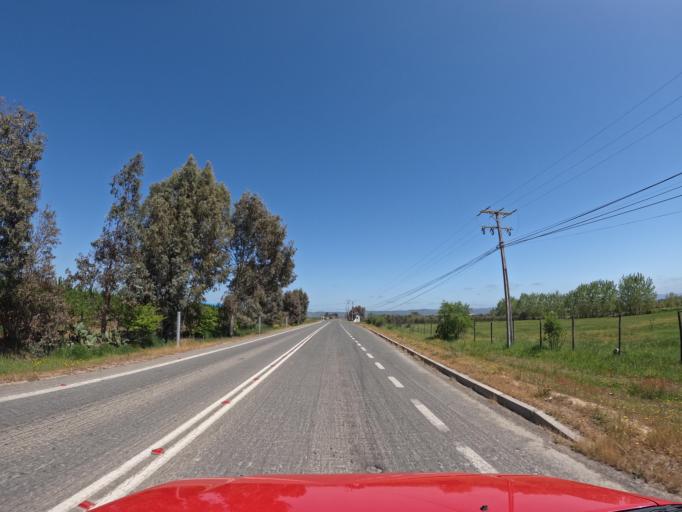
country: CL
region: O'Higgins
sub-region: Provincia de Colchagua
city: Santa Cruz
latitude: -34.7346
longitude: -71.6947
